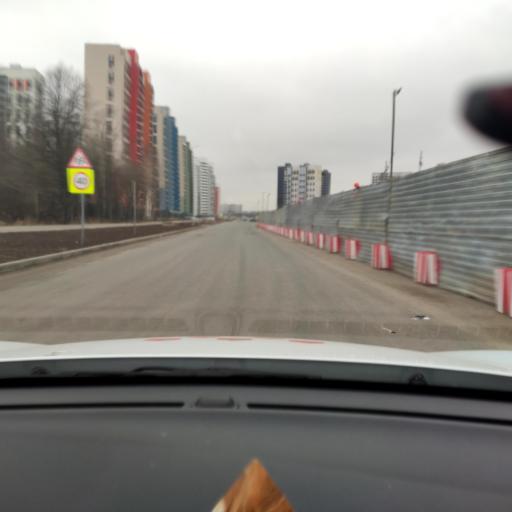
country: RU
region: Tatarstan
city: Osinovo
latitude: 55.8555
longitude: 48.9096
